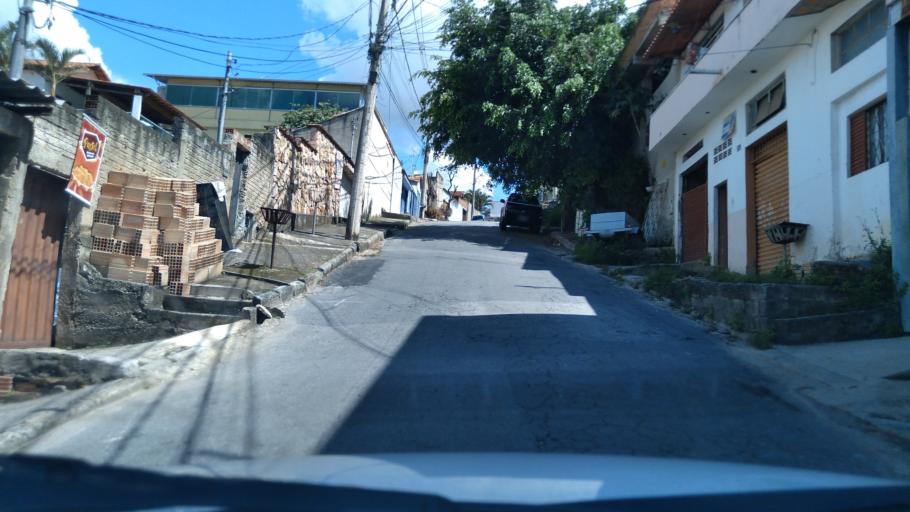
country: BR
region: Minas Gerais
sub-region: Belo Horizonte
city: Belo Horizonte
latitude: -19.8688
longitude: -43.9153
